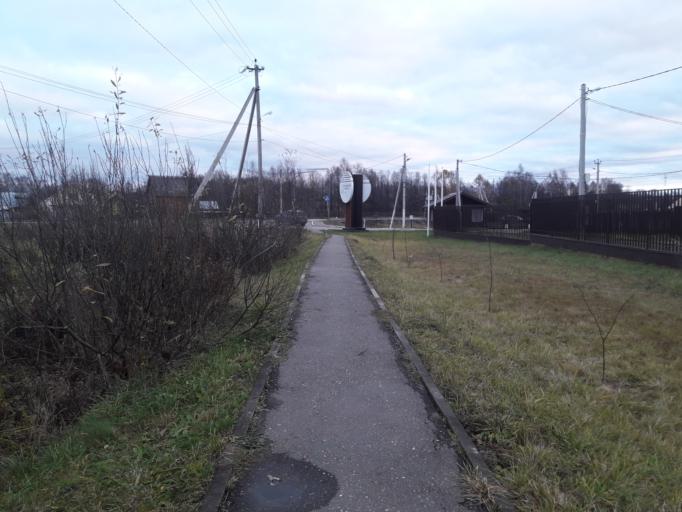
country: RU
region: Moskovskaya
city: Ashukino
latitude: 56.1718
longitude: 37.9389
